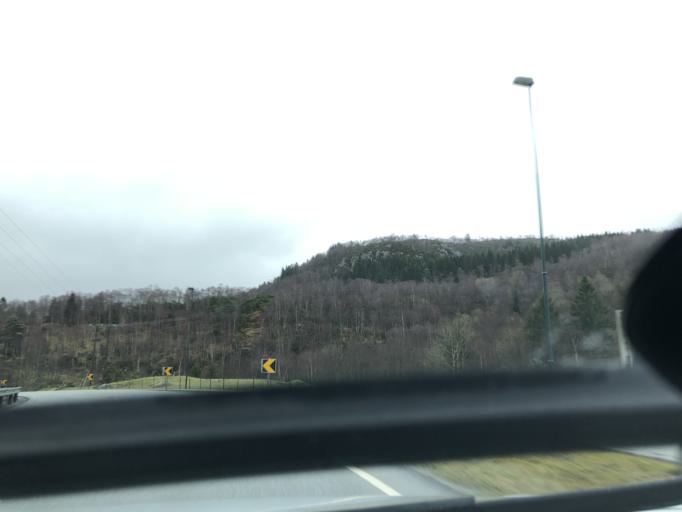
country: NO
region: Rogaland
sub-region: Hjelmeland
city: Hjelmelandsvagen
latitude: 59.2261
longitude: 6.1472
